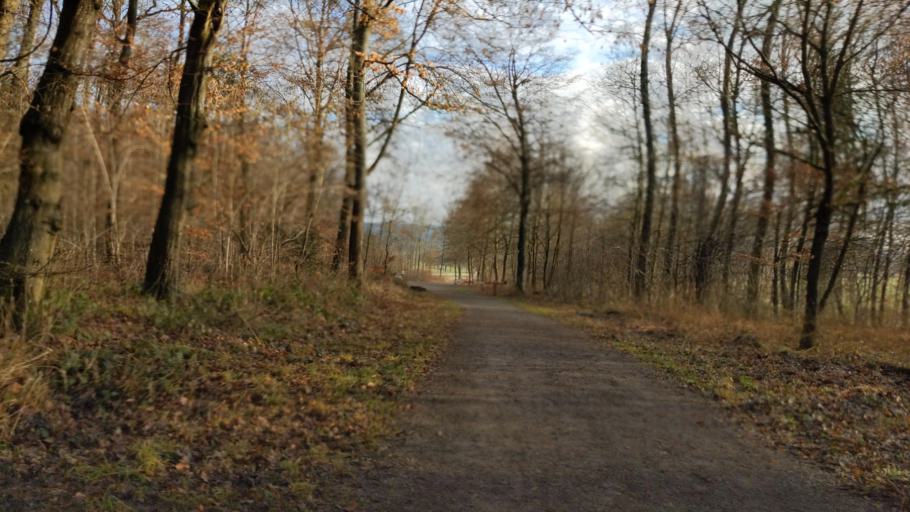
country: DE
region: Baden-Wuerttemberg
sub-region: Regierungsbezirk Stuttgart
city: Renningen
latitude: 48.7842
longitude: 8.9283
